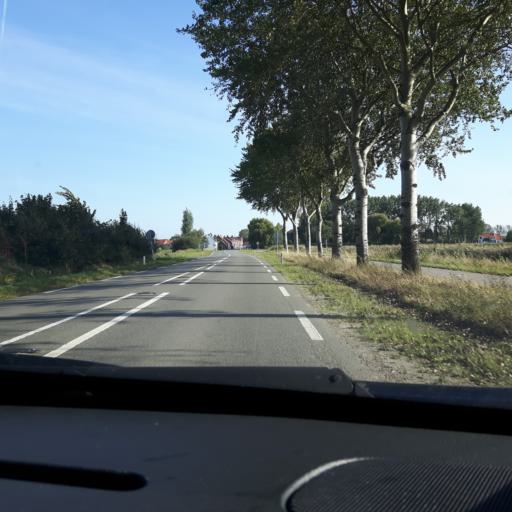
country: NL
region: Zeeland
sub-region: Gemeente Sluis
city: Sluis
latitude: 51.3445
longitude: 3.4457
